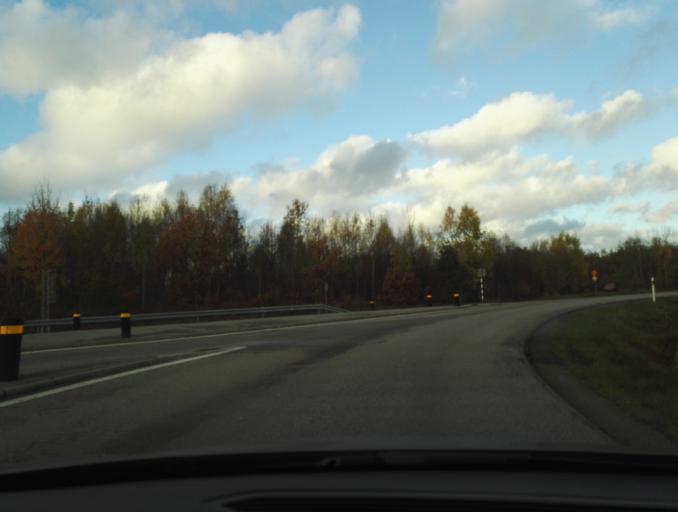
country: SE
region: Kronoberg
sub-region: Vaxjo Kommun
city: Vaexjoe
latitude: 56.9106
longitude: 14.7225
